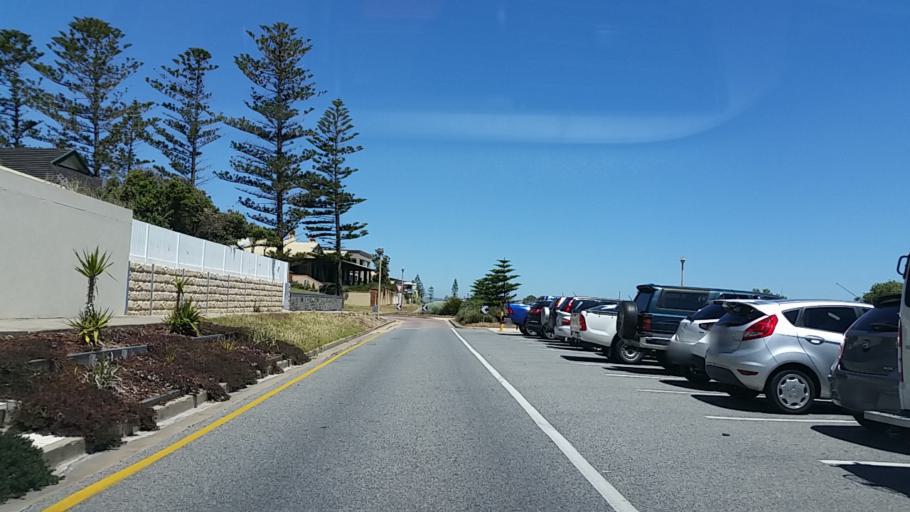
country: AU
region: South Australia
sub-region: Charles Sturt
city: Grange
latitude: -34.9046
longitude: 138.4898
